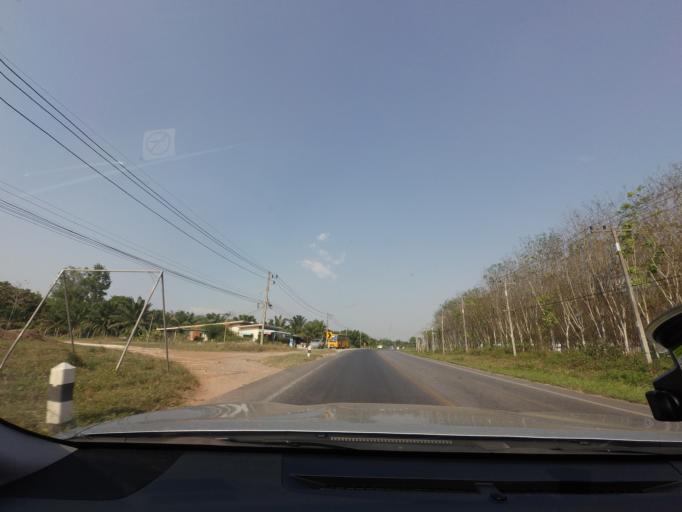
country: TH
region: Surat Thani
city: Phrasaeng
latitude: 8.5618
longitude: 99.1769
